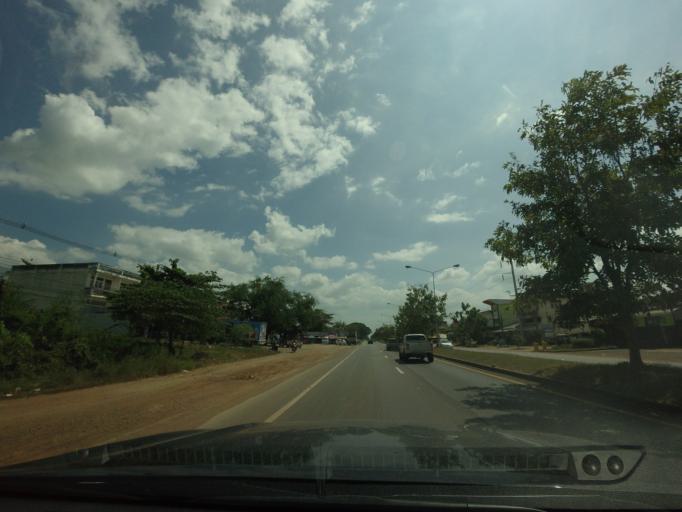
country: TH
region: Phetchabun
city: Nong Phai
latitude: 15.9155
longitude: 101.0264
